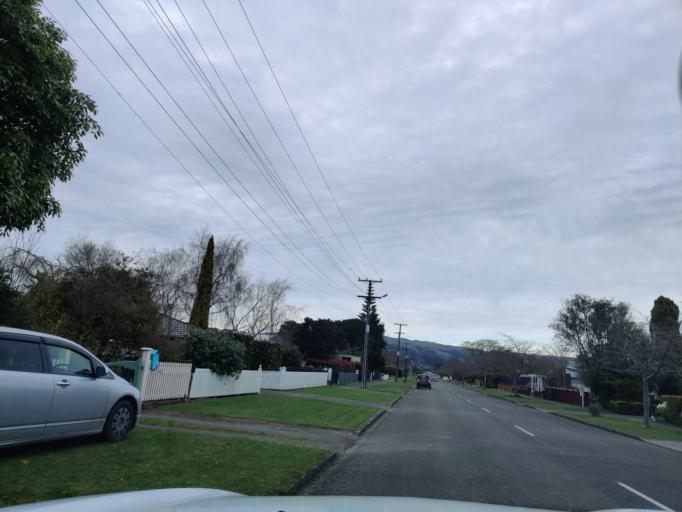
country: NZ
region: Manawatu-Wanganui
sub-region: Palmerston North City
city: Palmerston North
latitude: -40.2875
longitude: 175.7502
